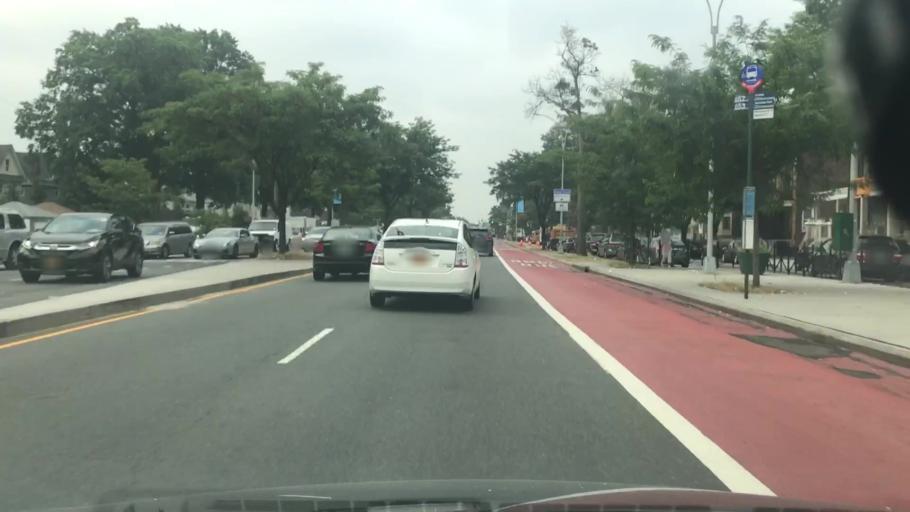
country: US
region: New York
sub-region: Queens County
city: Borough of Queens
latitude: 40.6933
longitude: -73.8521
